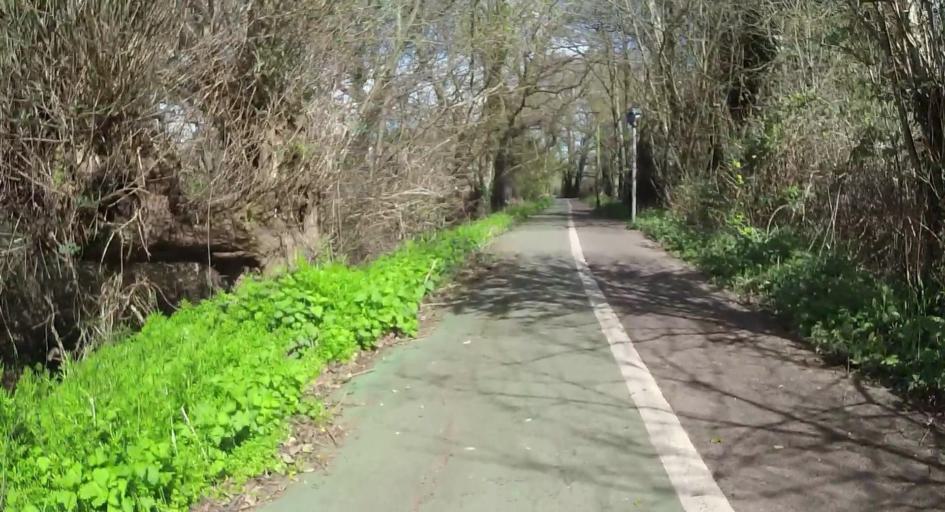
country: GB
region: England
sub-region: Surrey
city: Chertsey
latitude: 51.3813
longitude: -0.5031
